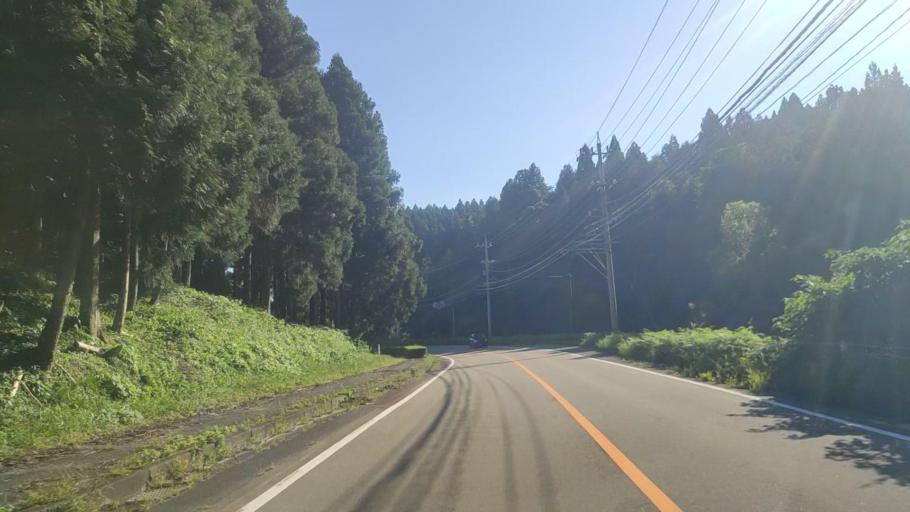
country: JP
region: Ishikawa
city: Nanao
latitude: 37.1205
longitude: 136.8621
